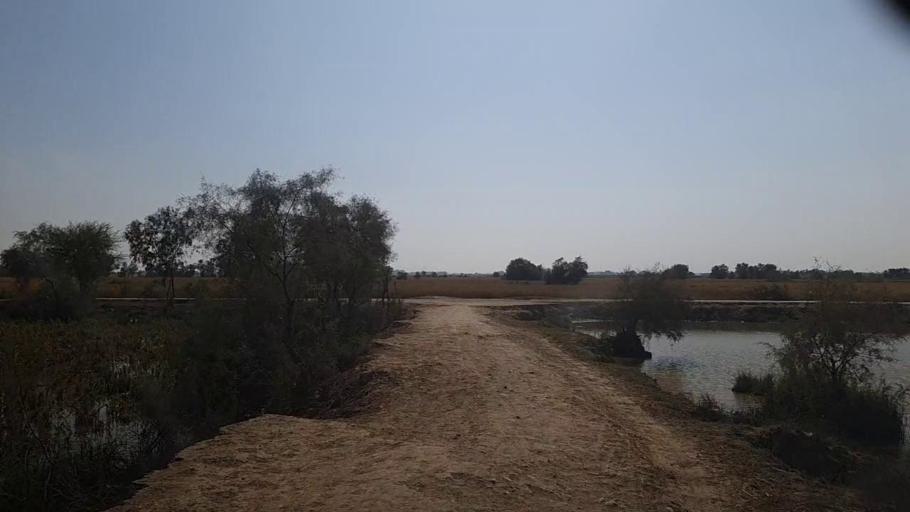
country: PK
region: Sindh
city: Thul
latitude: 28.1674
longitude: 68.7663
